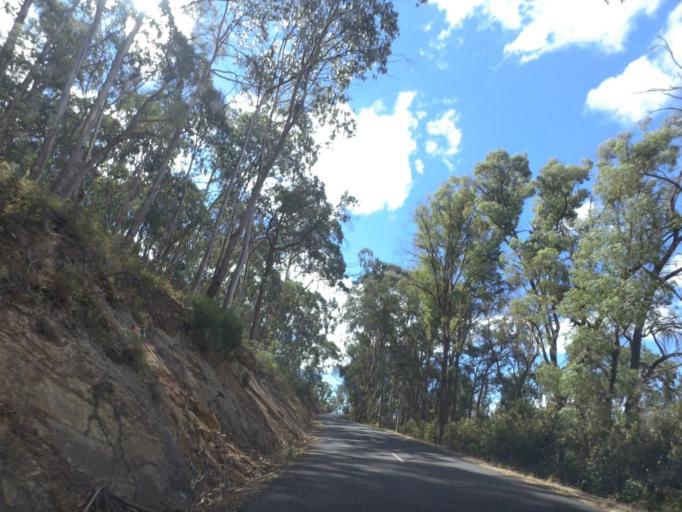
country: AU
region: Victoria
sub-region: Murrindindi
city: Alexandra
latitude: -37.3375
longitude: 145.9545
